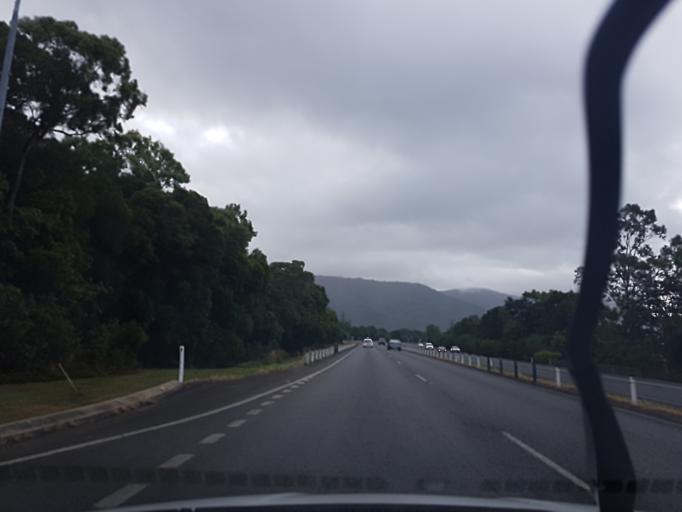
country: AU
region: Queensland
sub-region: Cairns
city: Trinity Beach
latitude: -16.7965
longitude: 145.6829
